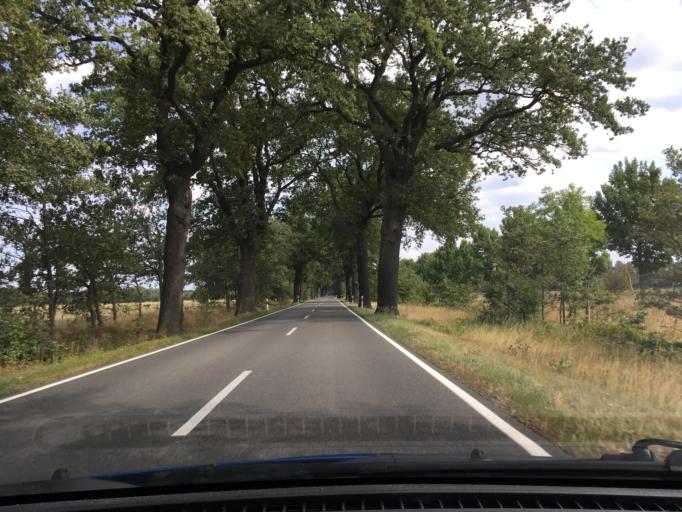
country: DE
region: Mecklenburg-Vorpommern
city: Eldena
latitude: 53.2485
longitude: 11.4343
